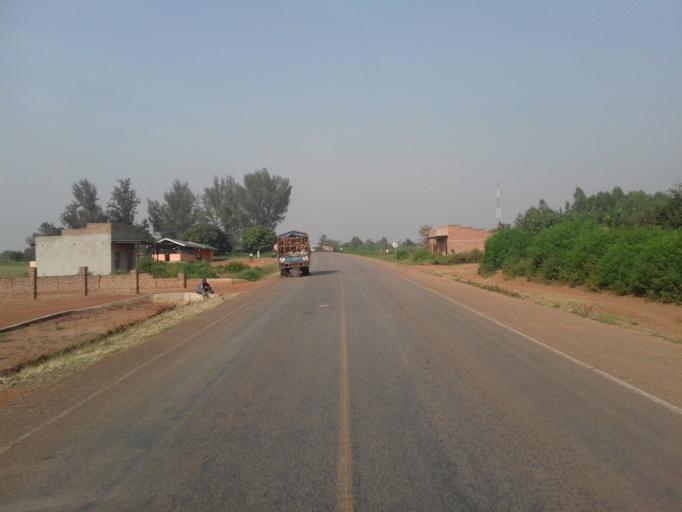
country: UG
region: Eastern Region
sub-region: Mbale District
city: Mbale
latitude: 1.0760
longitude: 34.1000
